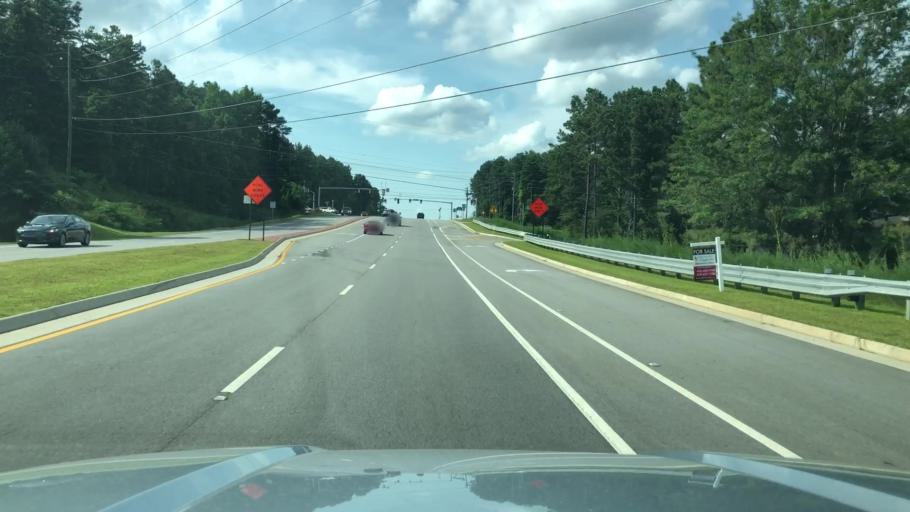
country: US
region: Georgia
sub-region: Paulding County
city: Hiram
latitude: 33.8668
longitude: -84.7807
